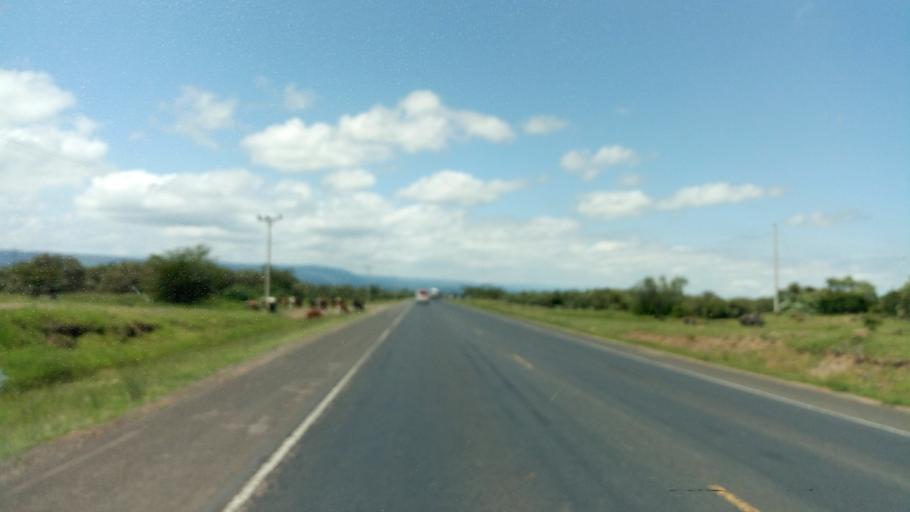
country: KE
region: Nakuru
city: Naivasha
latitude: -0.5448
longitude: 36.3419
